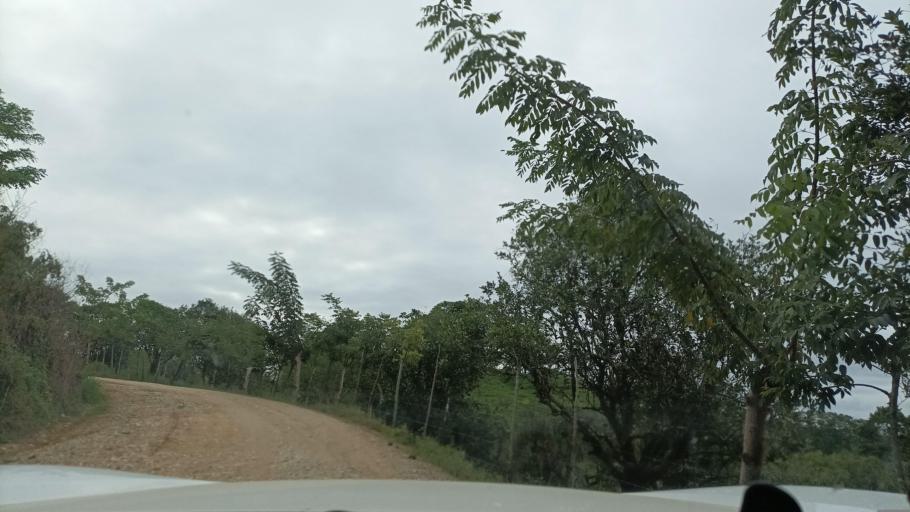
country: MX
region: Veracruz
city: Hidalgotitlan
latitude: 17.6027
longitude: -94.4265
